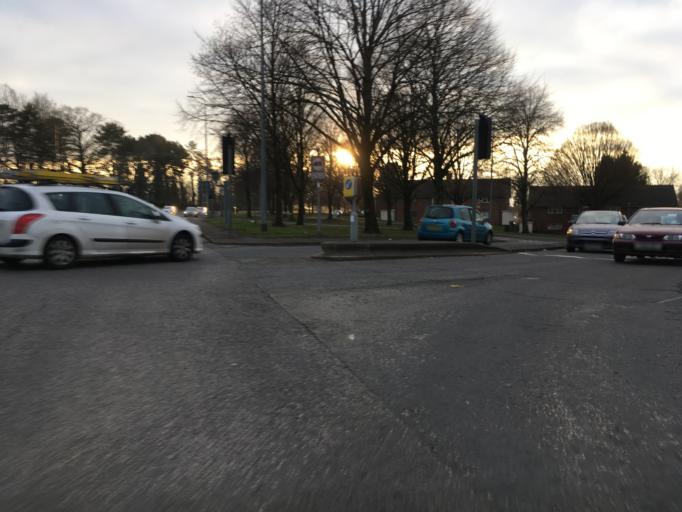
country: GB
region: Wales
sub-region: Newport
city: Marshfield
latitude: 51.5196
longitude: -3.1163
